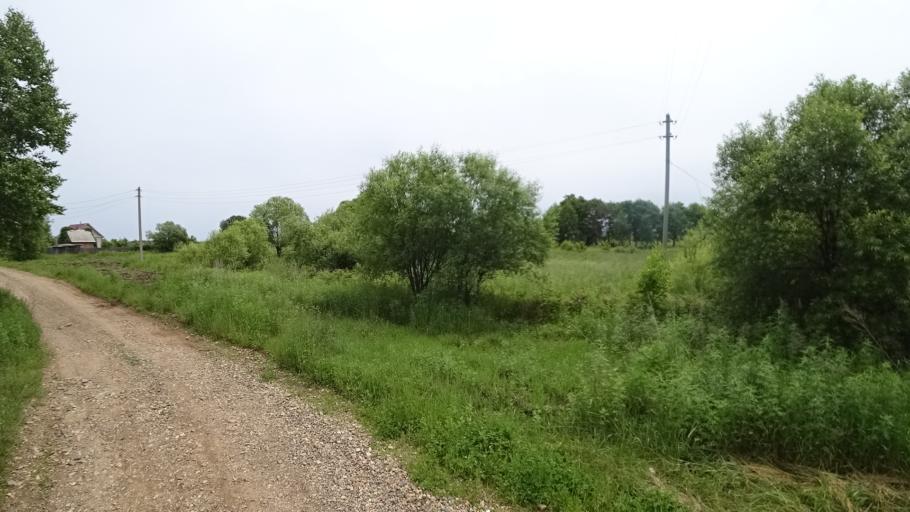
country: RU
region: Primorskiy
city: Arsen'yev
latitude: 44.1817
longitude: 133.3122
